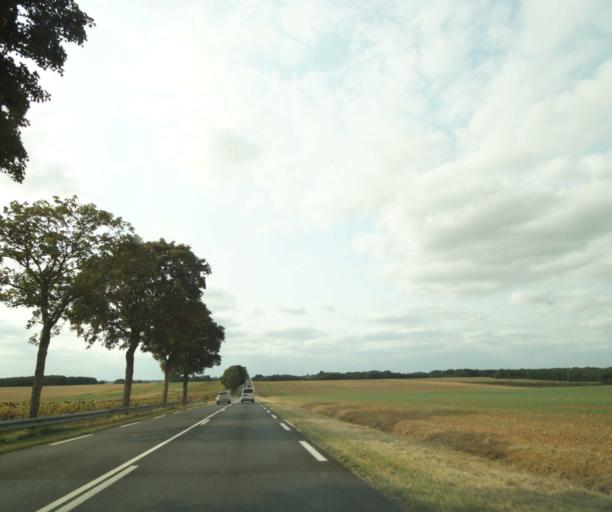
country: FR
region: Centre
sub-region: Departement d'Indre-et-Loire
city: Reignac-sur-Indre
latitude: 47.2258
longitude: 0.8814
